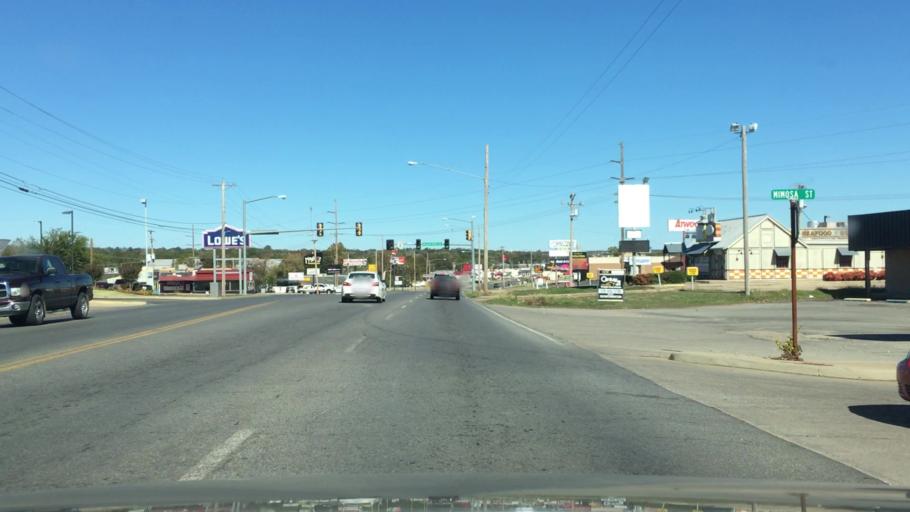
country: US
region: Oklahoma
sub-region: Cherokee County
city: Tahlequah
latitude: 35.8922
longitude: -94.9772
